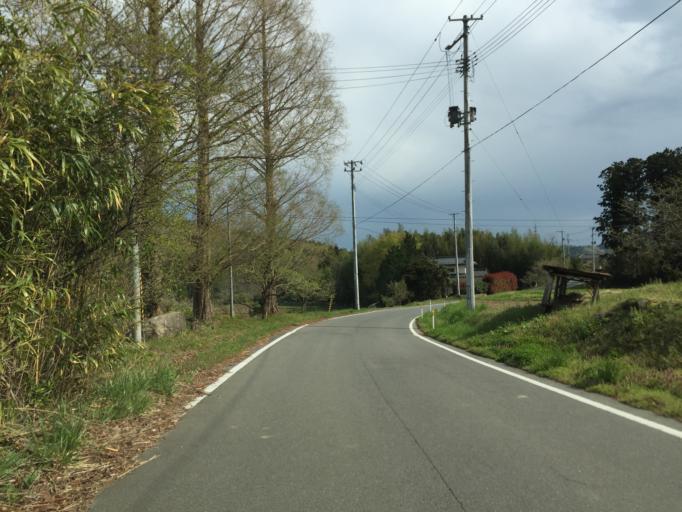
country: JP
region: Fukushima
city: Iwaki
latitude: 37.1272
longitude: 140.9025
